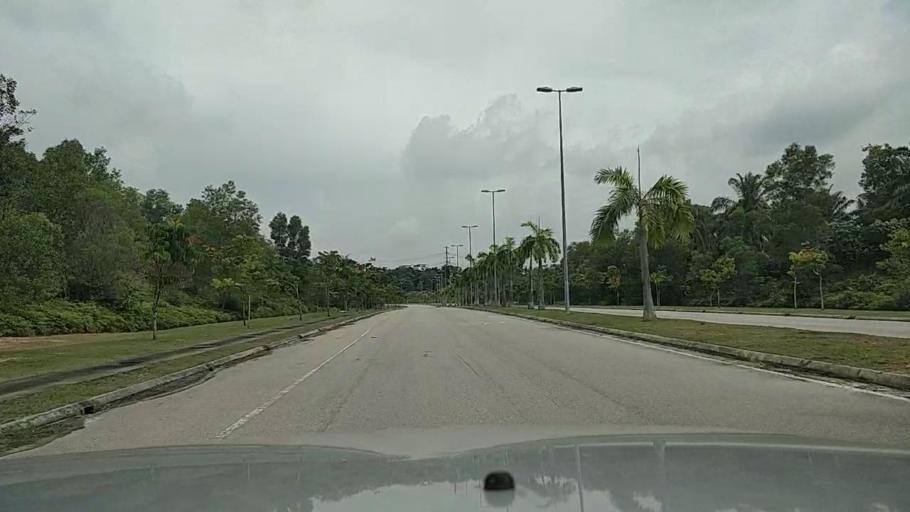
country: MY
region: Putrajaya
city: Putrajaya
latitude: 2.9006
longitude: 101.6484
